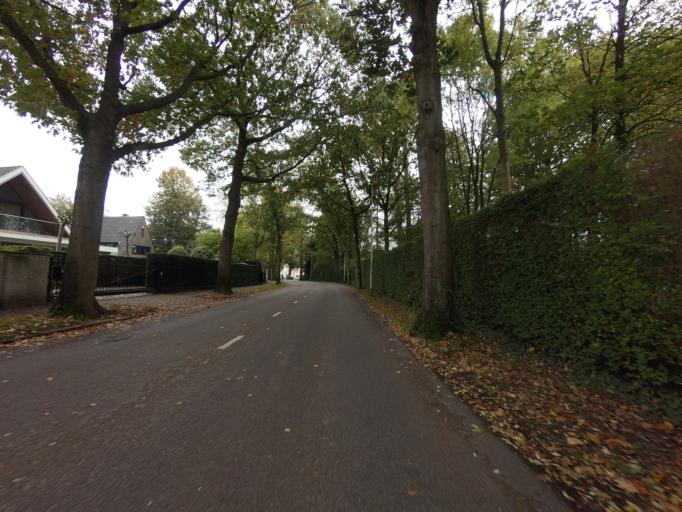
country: NL
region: North Brabant
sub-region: Gemeente Breda
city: Breda
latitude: 51.5633
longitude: 4.7896
